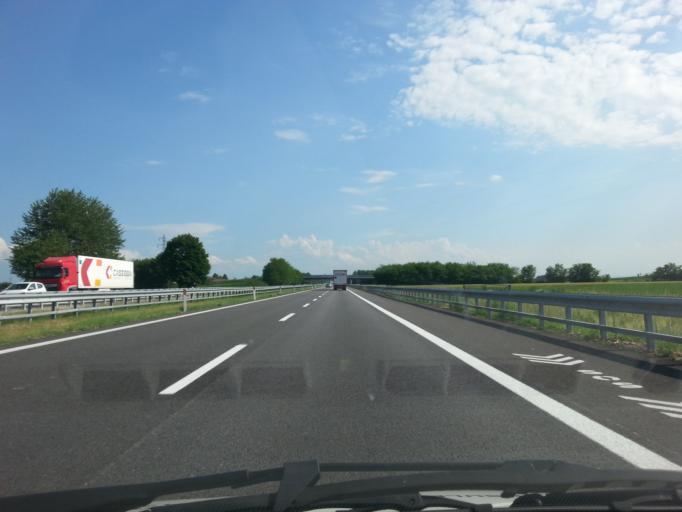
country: IT
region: Piedmont
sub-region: Provincia di Torino
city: Carmagnola
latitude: 44.8219
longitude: 7.7507
